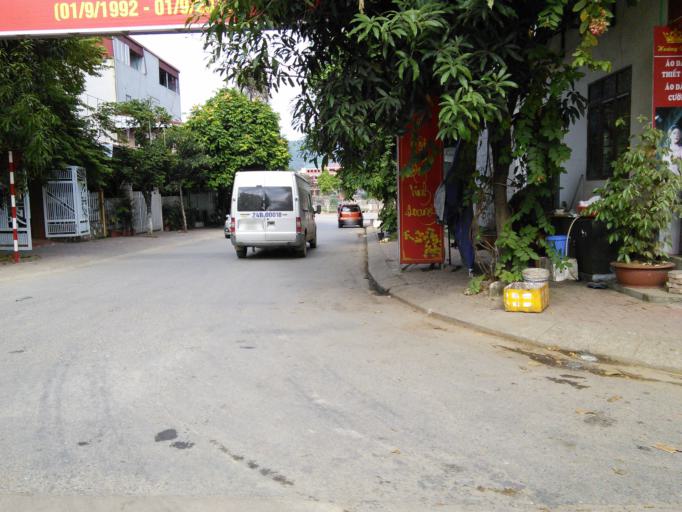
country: VN
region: Lao Cai
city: Lao Cai
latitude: 22.4856
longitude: 103.9750
